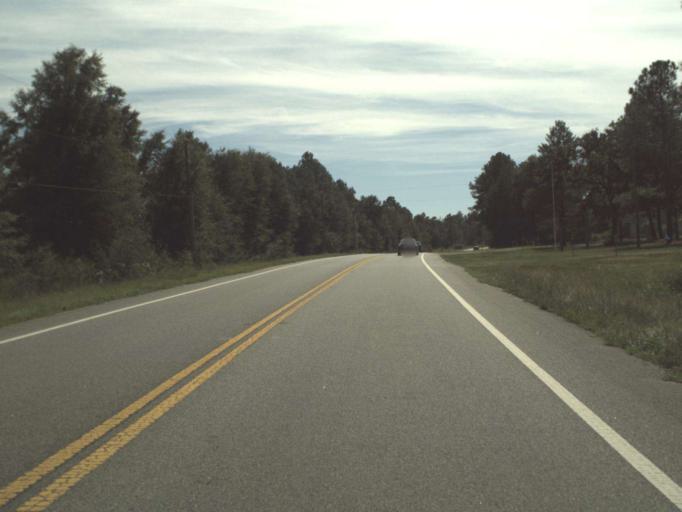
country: US
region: Florida
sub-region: Washington County
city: Chipley
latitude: 30.5919
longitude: -85.5922
